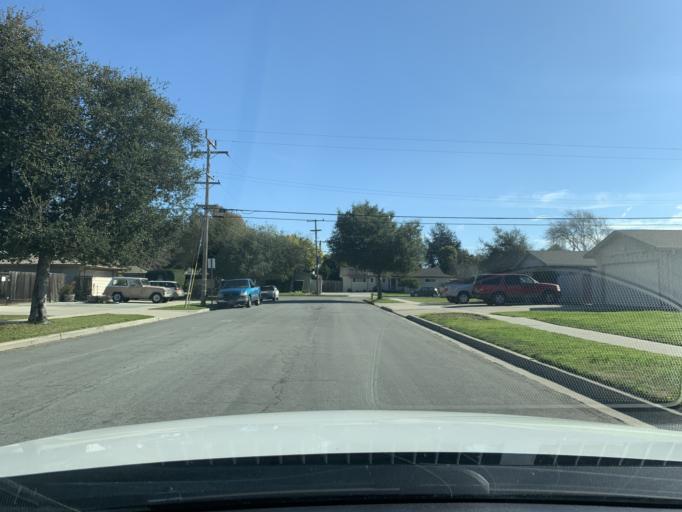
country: US
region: California
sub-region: Monterey County
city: Salinas
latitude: 36.6699
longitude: -121.6761
